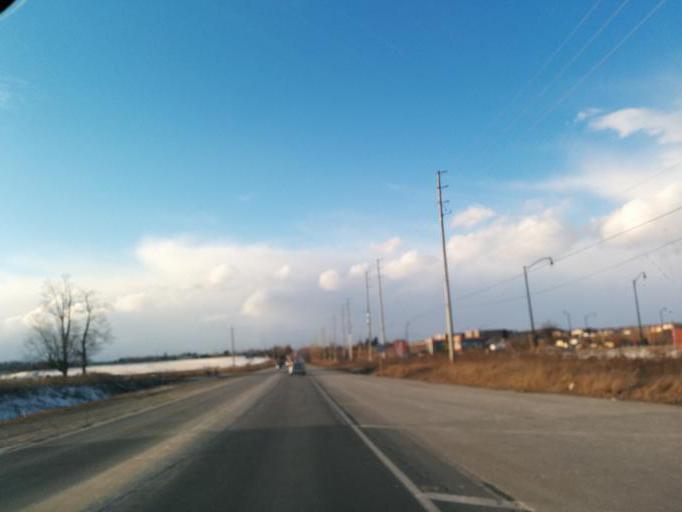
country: CA
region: Ontario
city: Brampton
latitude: 43.6613
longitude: -79.8217
